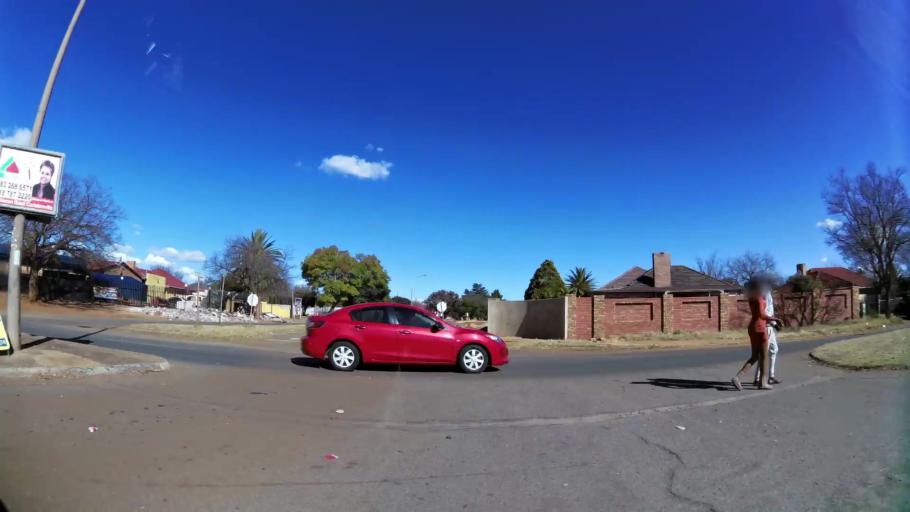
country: ZA
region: Gauteng
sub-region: West Rand District Municipality
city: Carletonville
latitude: -26.3601
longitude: 27.4000
